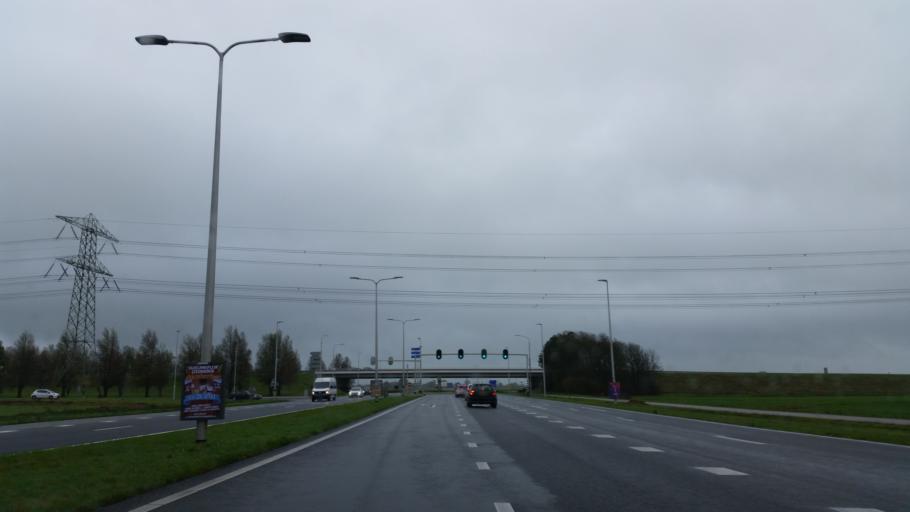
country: NL
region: Friesland
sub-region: Gemeente Boarnsterhim
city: Wergea
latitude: 53.1692
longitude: 5.8283
